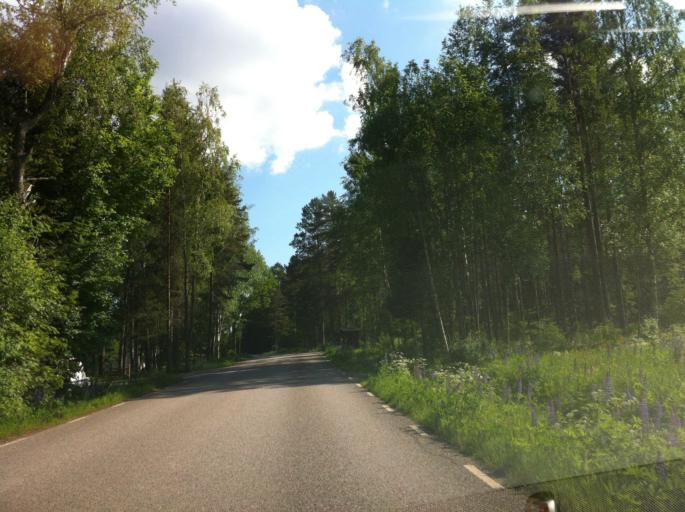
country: SE
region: Vaermland
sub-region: Sunne Kommun
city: Sunne
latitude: 59.7164
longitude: 13.2266
